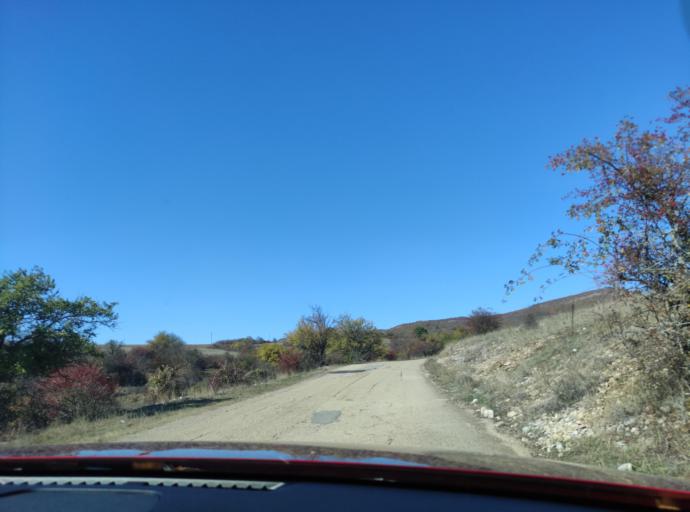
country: BG
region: Montana
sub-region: Obshtina Montana
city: Montana
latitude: 43.4421
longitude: 23.0508
